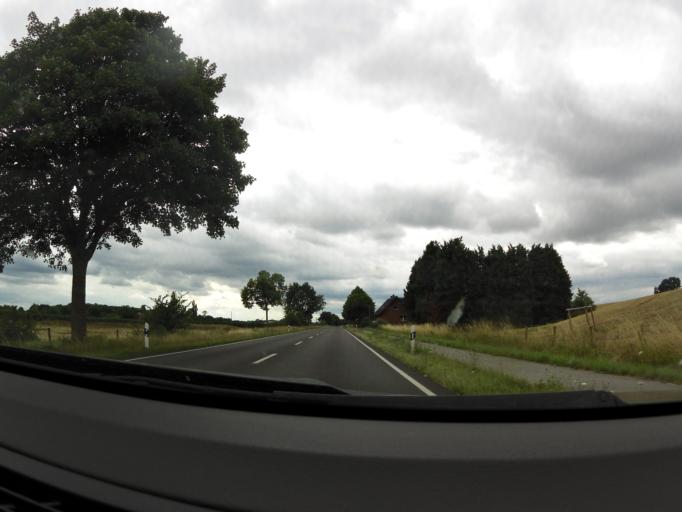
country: DE
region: North Rhine-Westphalia
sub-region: Regierungsbezirk Dusseldorf
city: Alpen
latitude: 51.6342
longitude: 6.5138
